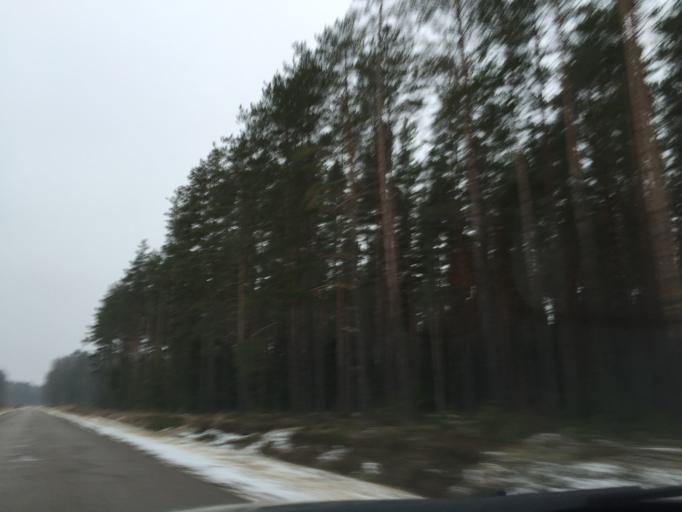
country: LV
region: Saulkrastu
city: Saulkrasti
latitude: 57.4934
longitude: 24.4239
